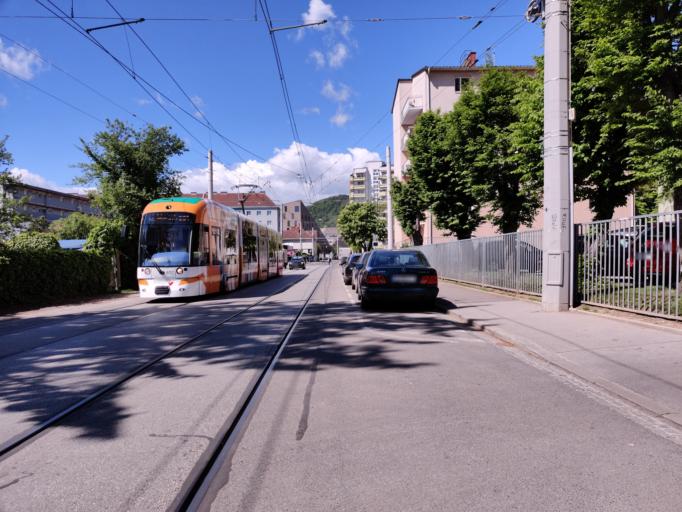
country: AT
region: Styria
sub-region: Graz Stadt
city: Wetzelsdorf
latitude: 47.0734
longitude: 15.4110
